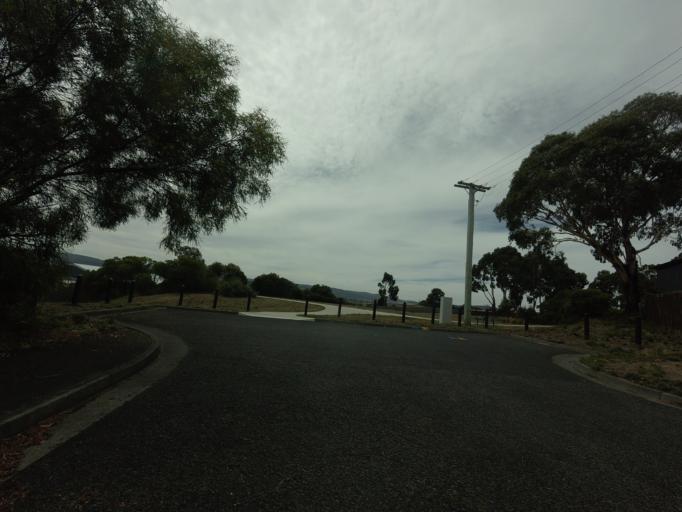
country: AU
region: Tasmania
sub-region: Sorell
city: Sorell
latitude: -42.7956
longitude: 147.5287
